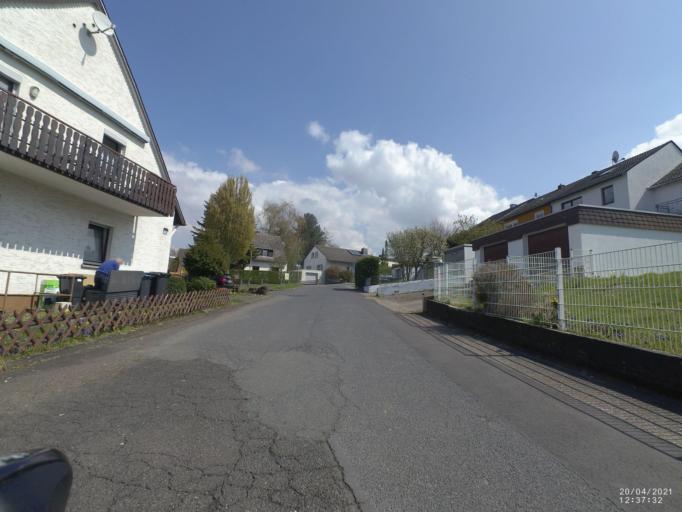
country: DE
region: Rheinland-Pfalz
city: Niederwerth
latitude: 50.4070
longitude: 7.6159
